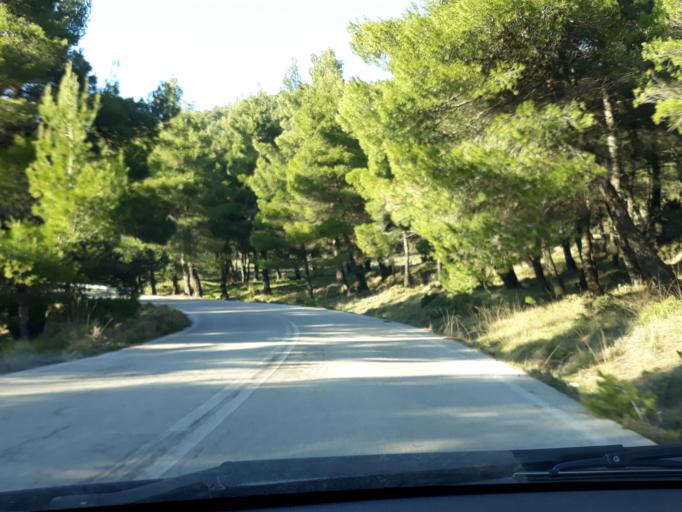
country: GR
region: Attica
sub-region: Nomarchia Dytikis Attikis
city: Fyli
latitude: 38.1485
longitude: 23.6346
